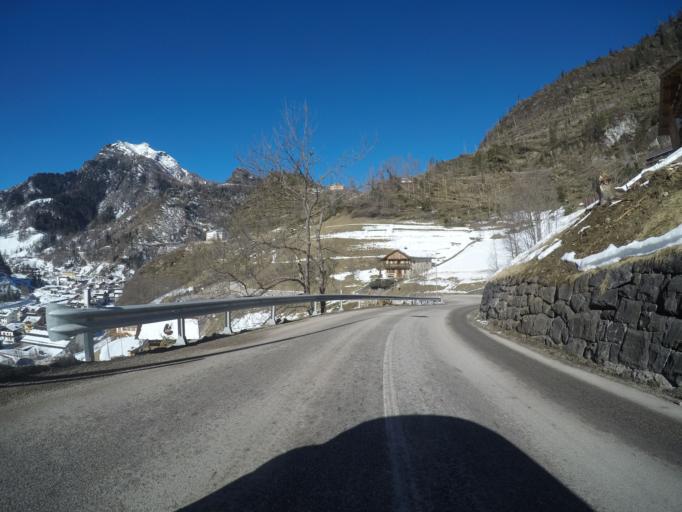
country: IT
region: Veneto
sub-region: Provincia di Belluno
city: Colle Santa Lucia
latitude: 46.4394
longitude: 11.9968
